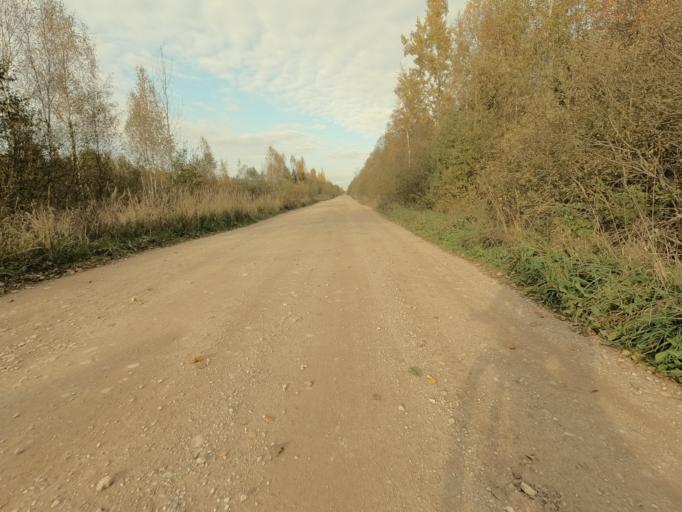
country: RU
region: Novgorod
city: Volkhovskiy
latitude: 58.9075
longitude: 31.0376
